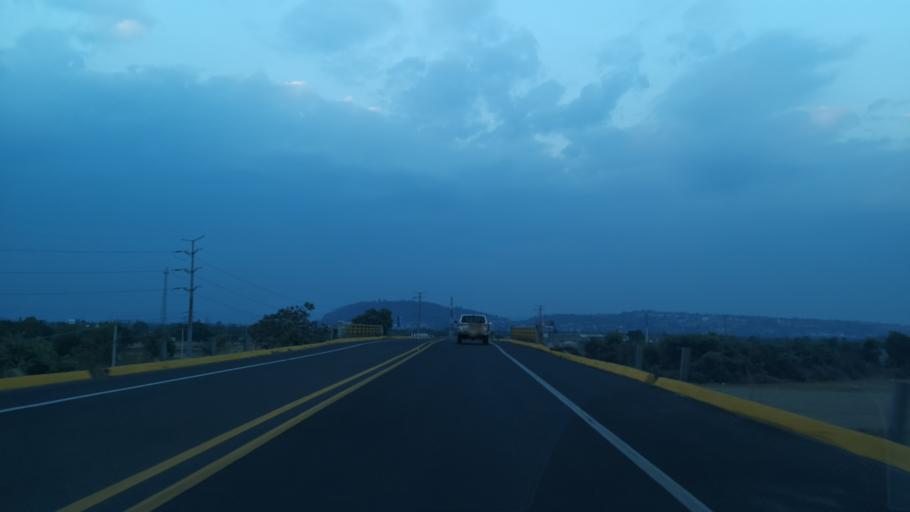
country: MX
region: Puebla
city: Santa Ana Xalmimilulco
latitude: 19.2077
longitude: -98.3608
